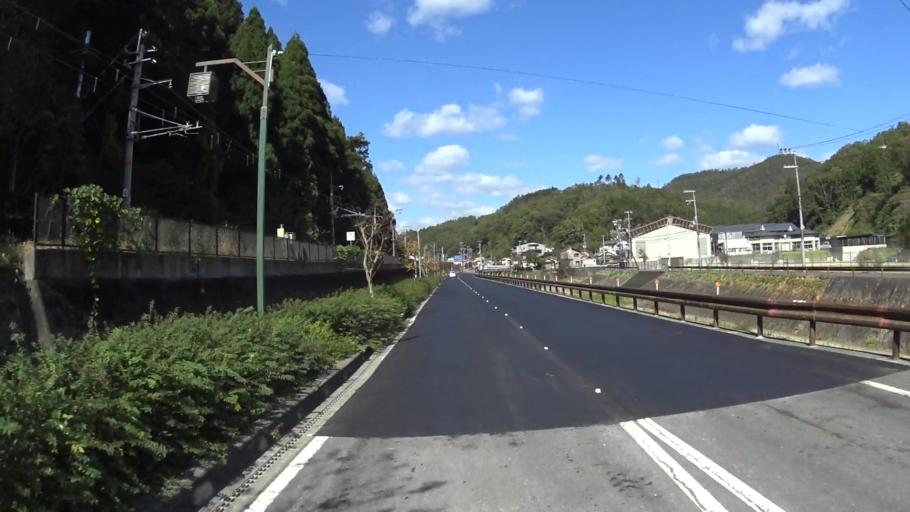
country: JP
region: Kyoto
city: Kameoka
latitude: 35.1588
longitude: 135.5059
